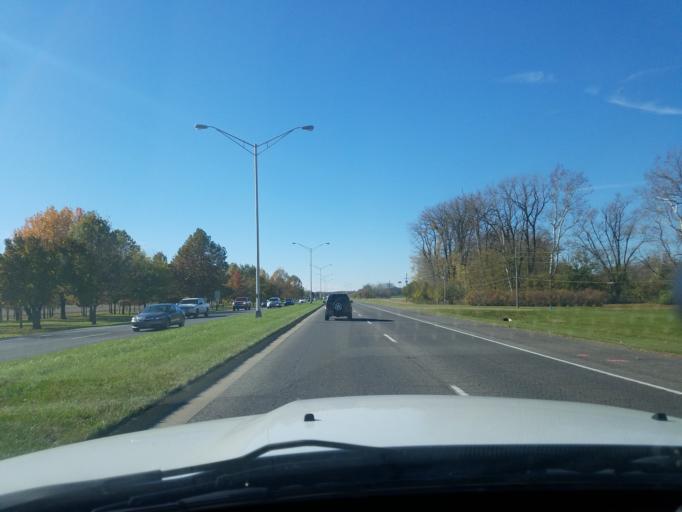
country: US
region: Indiana
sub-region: Bartholomew County
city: Columbus
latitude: 39.1997
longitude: -85.9385
